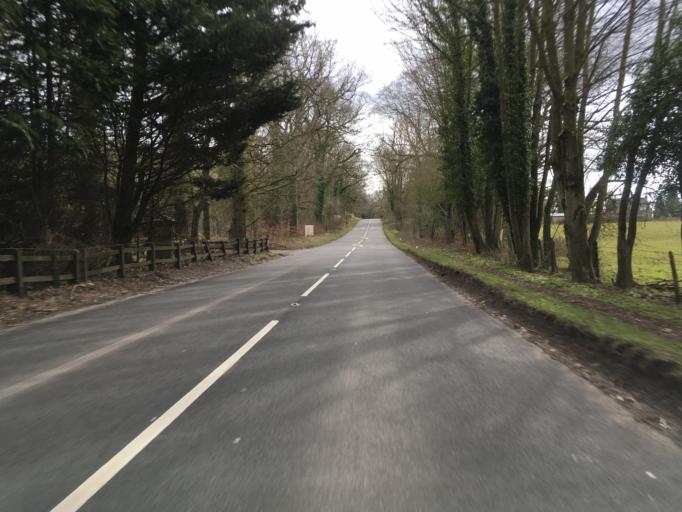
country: GB
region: England
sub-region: Gloucestershire
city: Coleford
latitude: 51.7788
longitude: -2.6099
